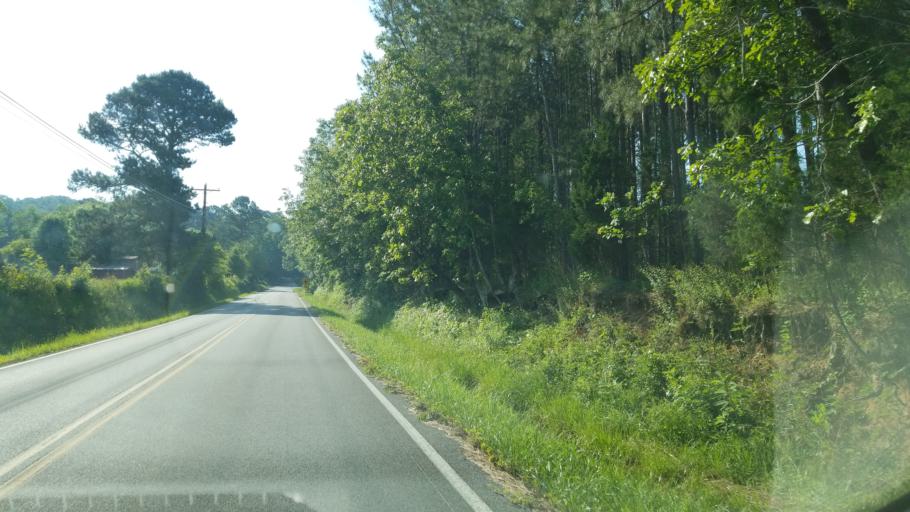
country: US
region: Tennessee
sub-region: Hamilton County
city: Collegedale
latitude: 35.0773
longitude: -85.0011
